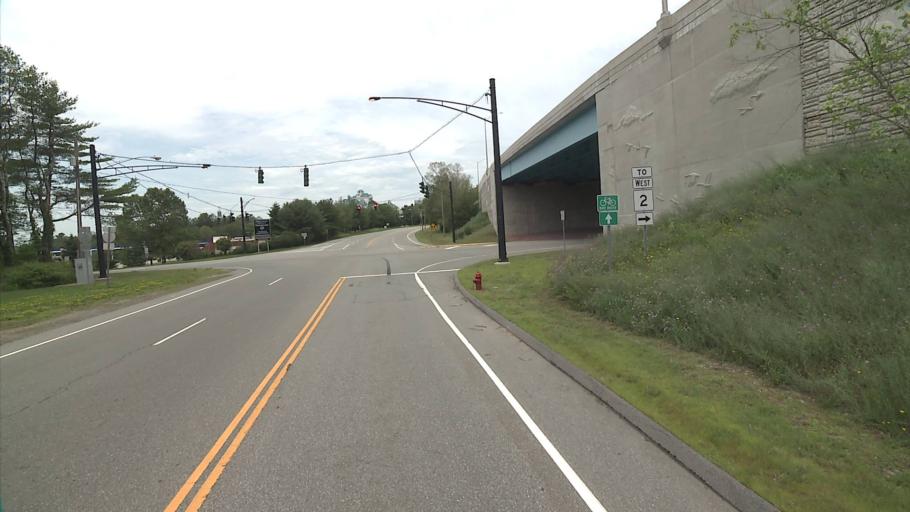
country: US
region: Connecticut
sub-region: New London County
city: Preston City
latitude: 41.4699
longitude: -71.9505
